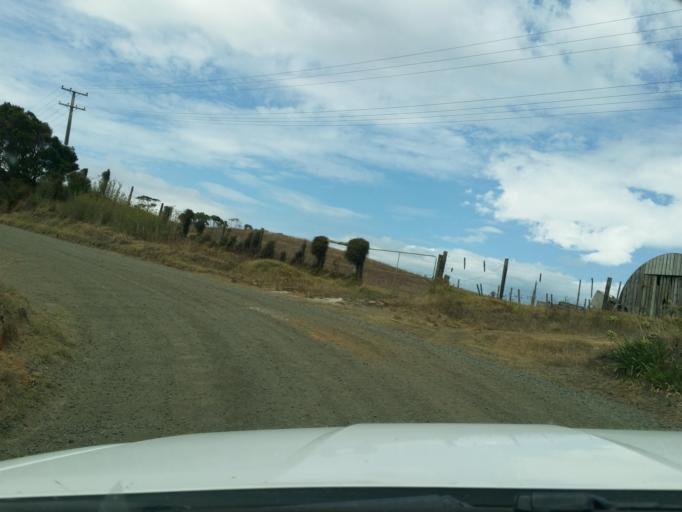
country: NZ
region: Auckland
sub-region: Auckland
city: Wellsford
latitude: -36.3454
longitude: 174.1677
